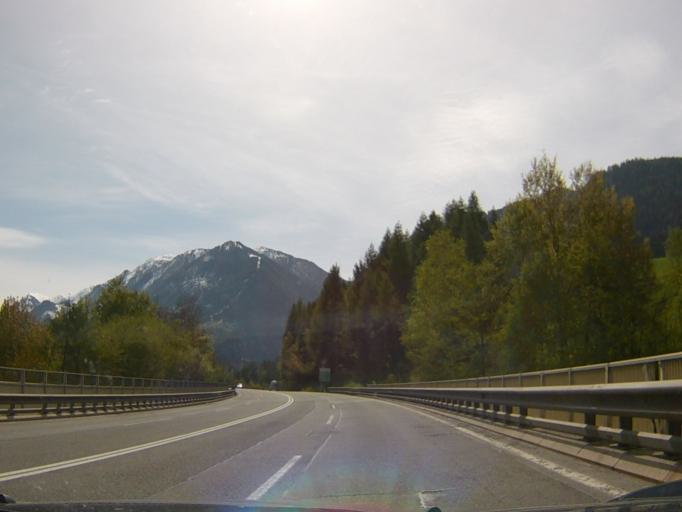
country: AT
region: Salzburg
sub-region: Politischer Bezirk Zell am See
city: Lend
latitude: 47.3012
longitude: 13.0354
